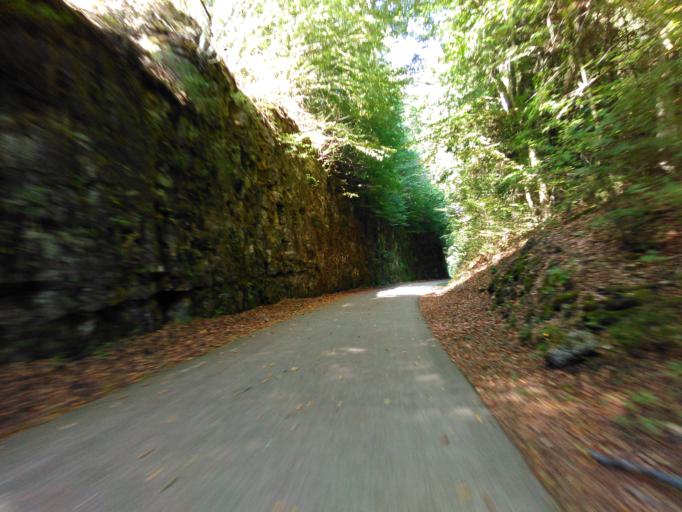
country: LU
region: Luxembourg
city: Eischen
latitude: 49.6697
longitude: 5.8941
